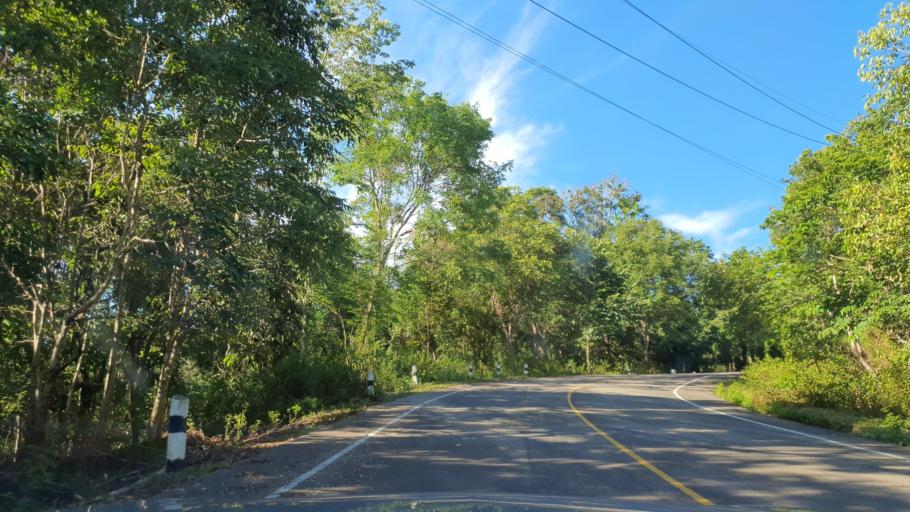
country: TH
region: Chiang Mai
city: Mae On
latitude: 18.8024
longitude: 99.3039
